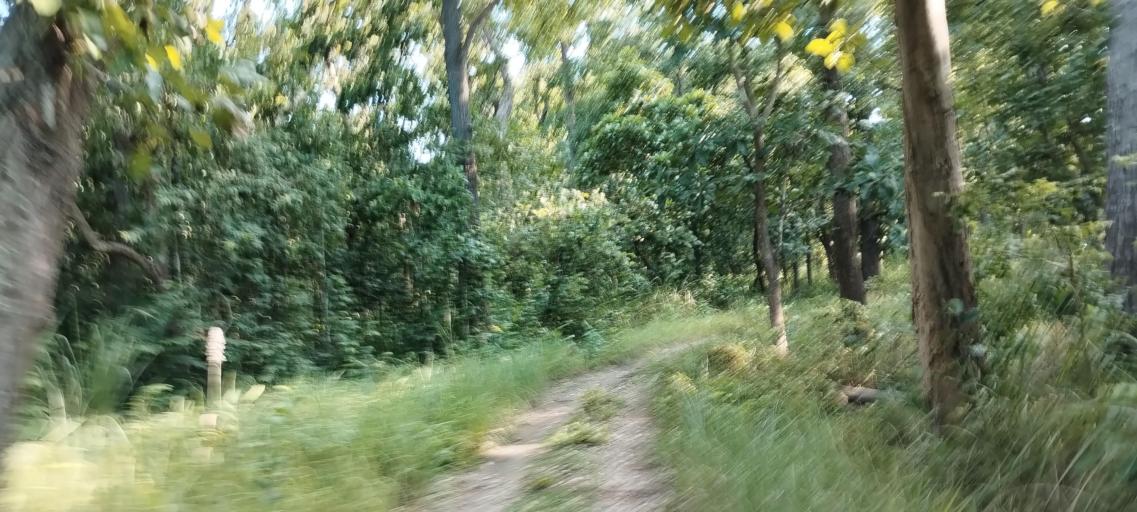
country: NP
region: Far Western
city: Tikapur
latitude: 28.5183
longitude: 81.2750
